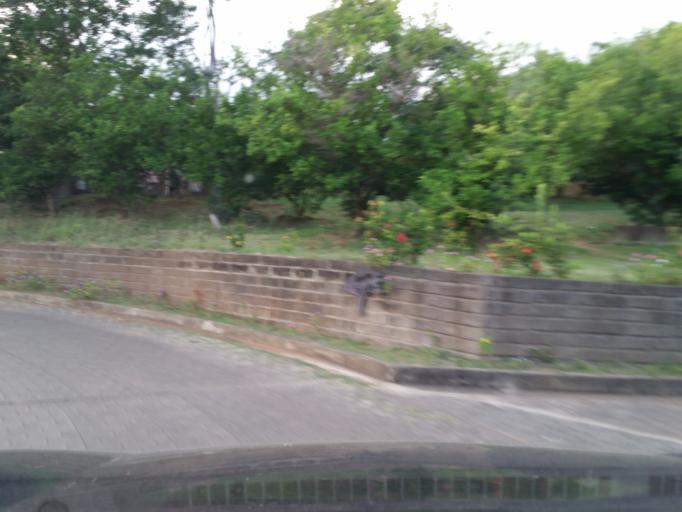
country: NI
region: Rivas
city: San Juan del Sur
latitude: 11.2672
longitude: -85.8587
